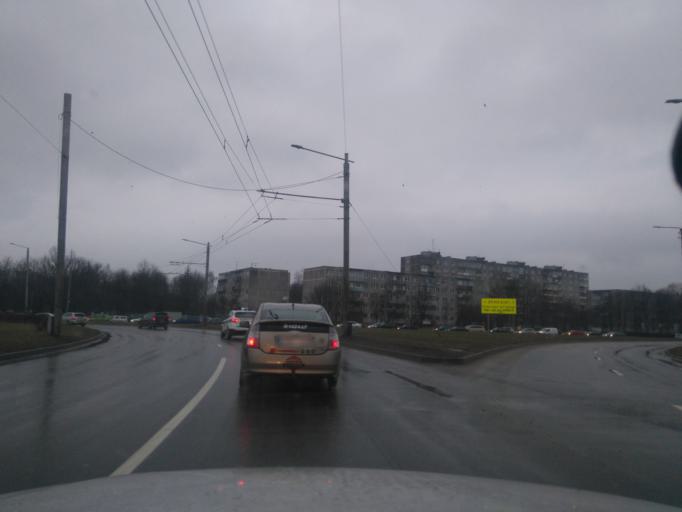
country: LT
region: Kauno apskritis
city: Dainava (Kaunas)
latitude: 54.9128
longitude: 23.9758
